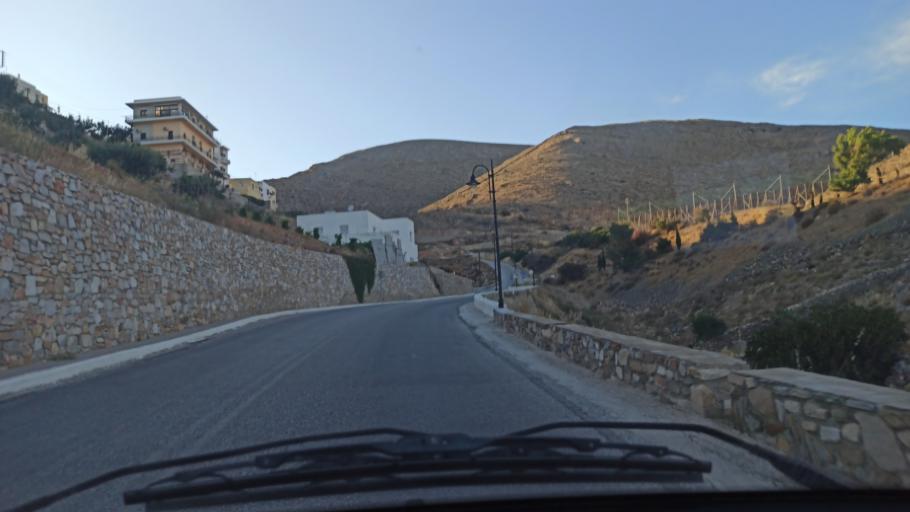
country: GR
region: South Aegean
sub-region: Nomos Kykladon
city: Ano Syros
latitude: 37.4515
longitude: 24.9370
